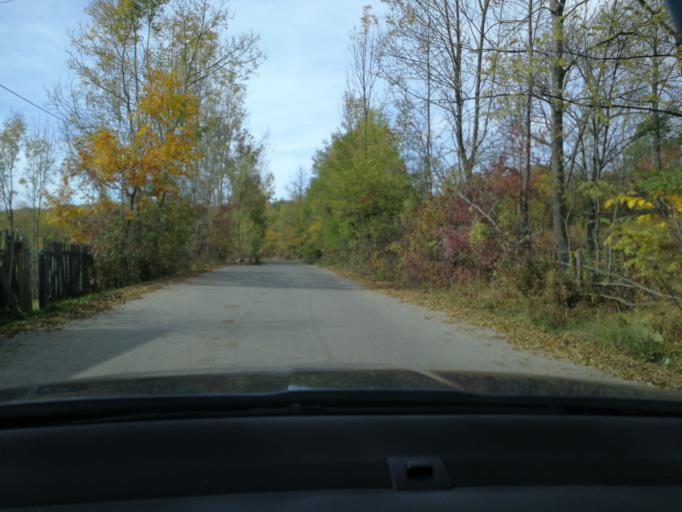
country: RO
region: Prahova
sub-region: Comuna Brebu
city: Pietriceaua
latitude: 45.2063
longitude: 25.7933
